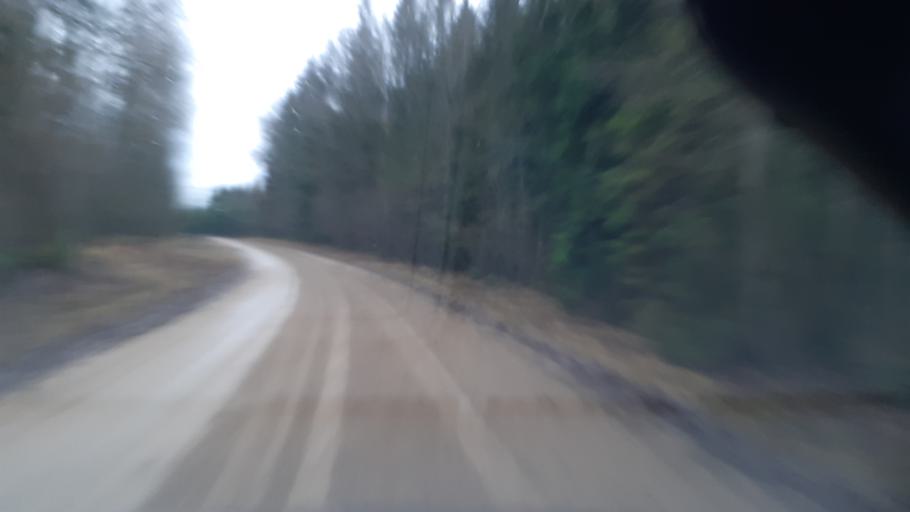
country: LV
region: Kuldigas Rajons
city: Kuldiga
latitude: 56.9159
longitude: 21.7703
